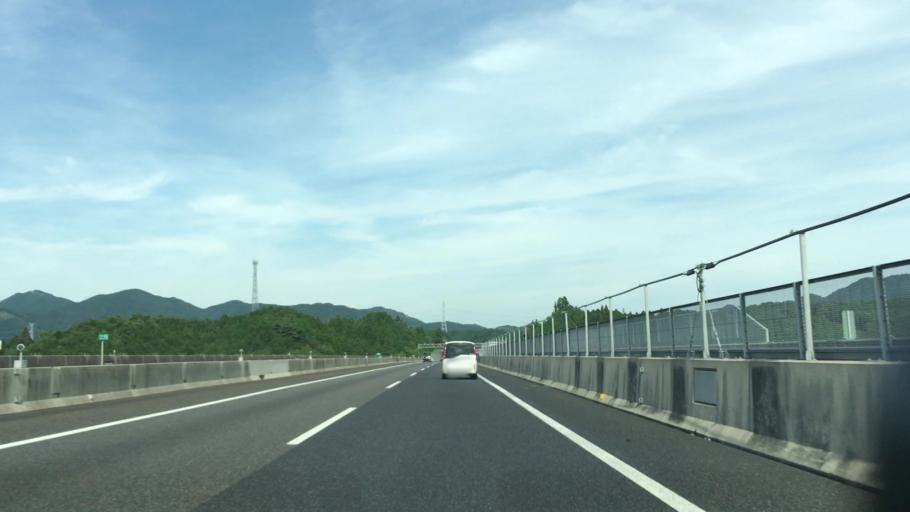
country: JP
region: Shiga Prefecture
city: Hino
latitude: 34.9154
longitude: 136.3174
